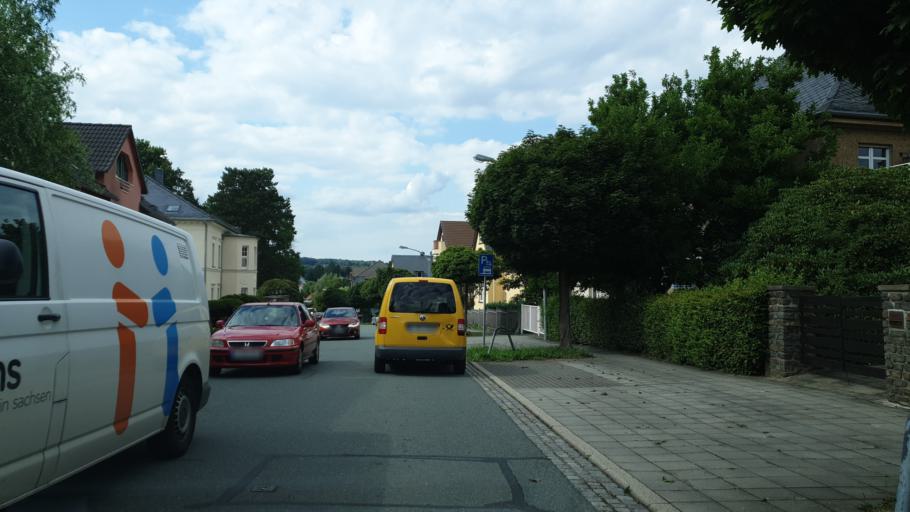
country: DE
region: Saxony
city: Neukirchen
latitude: 50.8109
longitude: 12.8323
